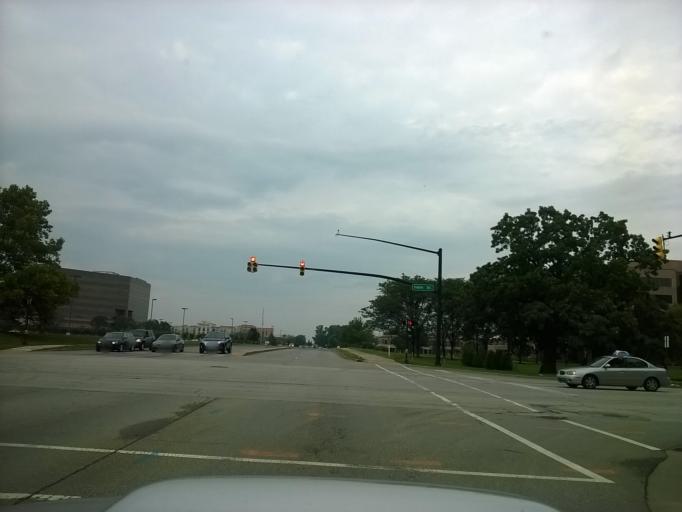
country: US
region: Indiana
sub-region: Hamilton County
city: Carmel
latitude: 39.9561
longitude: -86.1551
